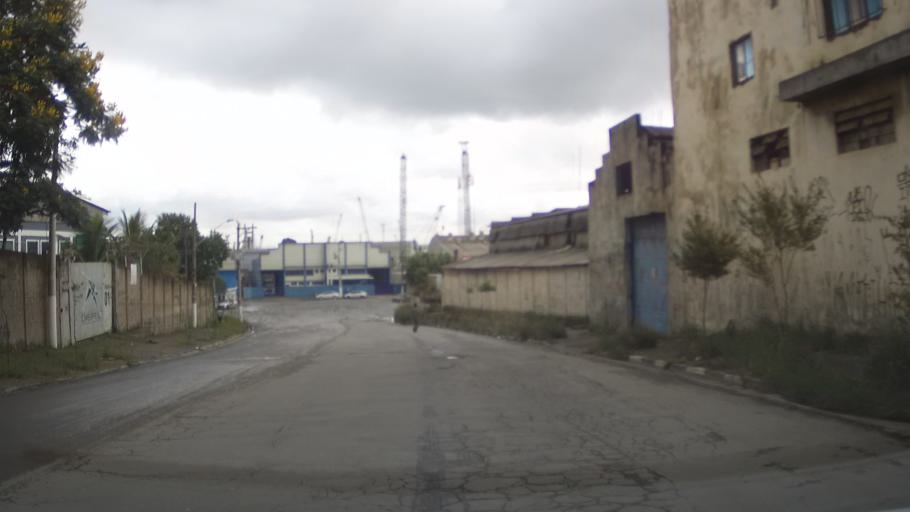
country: BR
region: Sao Paulo
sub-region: Guarulhos
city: Guarulhos
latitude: -23.4636
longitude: -46.4841
